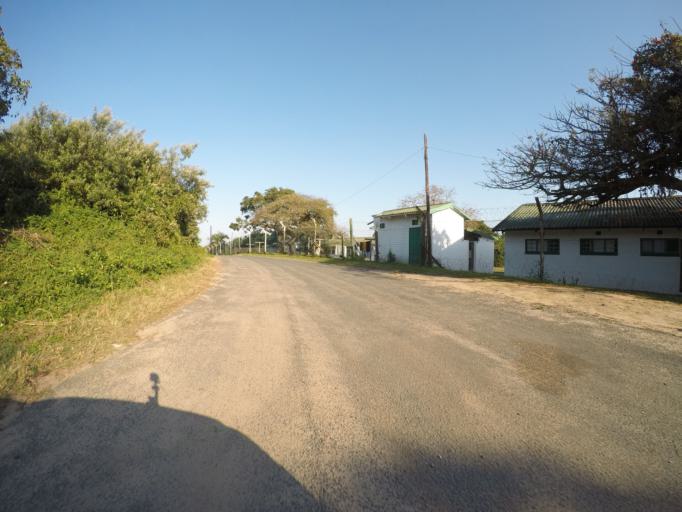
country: ZA
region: KwaZulu-Natal
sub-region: uThungulu District Municipality
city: Richards Bay
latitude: -28.7817
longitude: 32.0877
